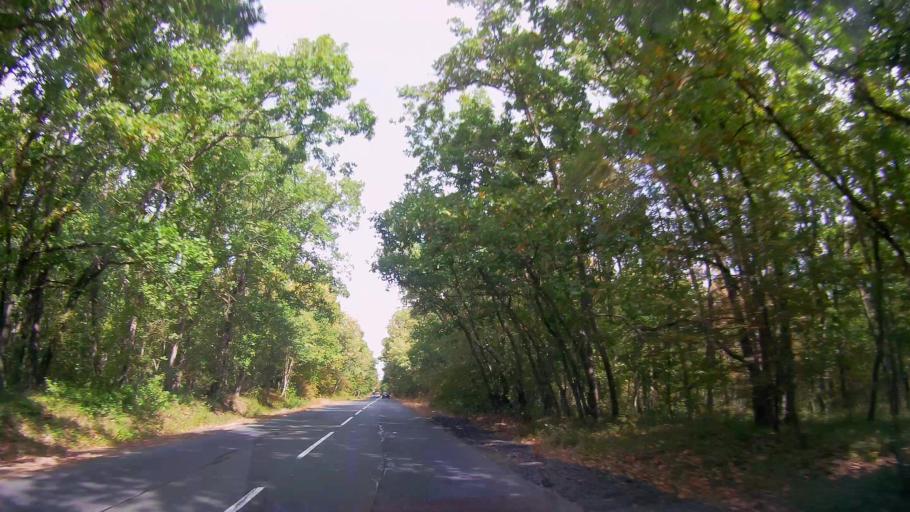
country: BG
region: Burgas
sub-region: Obshtina Primorsko
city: Primorsko
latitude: 42.2883
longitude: 27.7355
